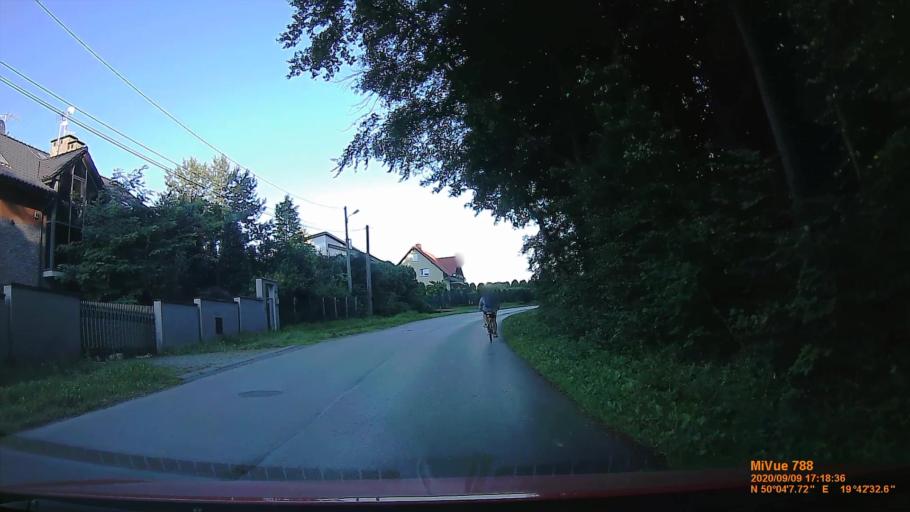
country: PL
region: Lesser Poland Voivodeship
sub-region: Powiat krakowski
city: Czulow
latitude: 50.0688
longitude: 19.7091
